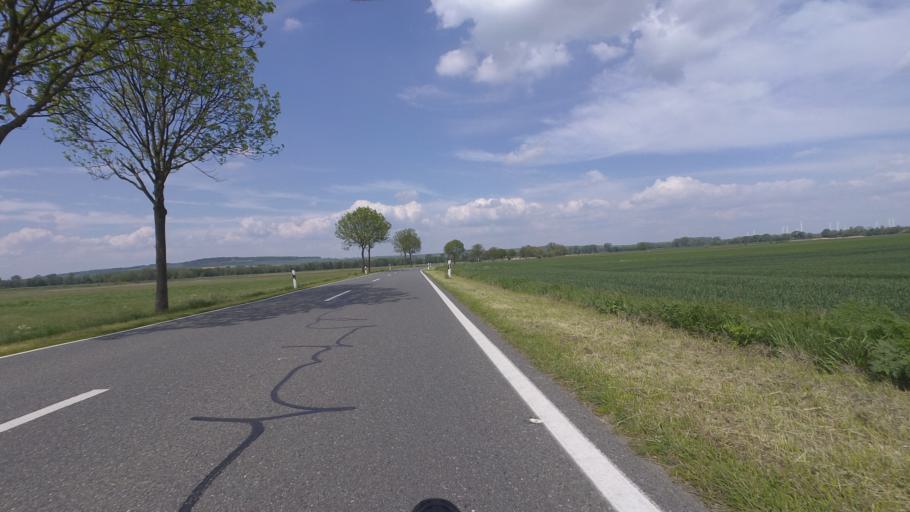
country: DE
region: Lower Saxony
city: Jerxheim
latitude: 52.0530
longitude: 10.8837
